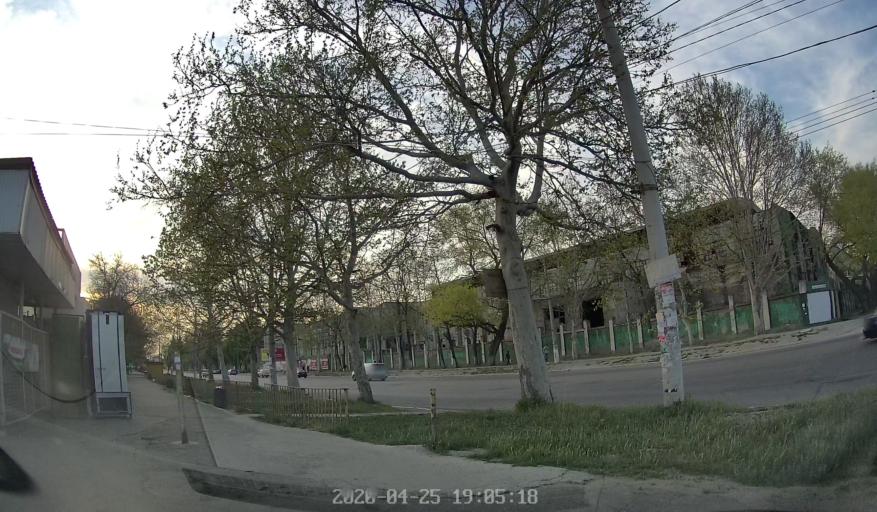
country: NG
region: Niger
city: Lemu
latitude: 9.2937
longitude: 6.1350
